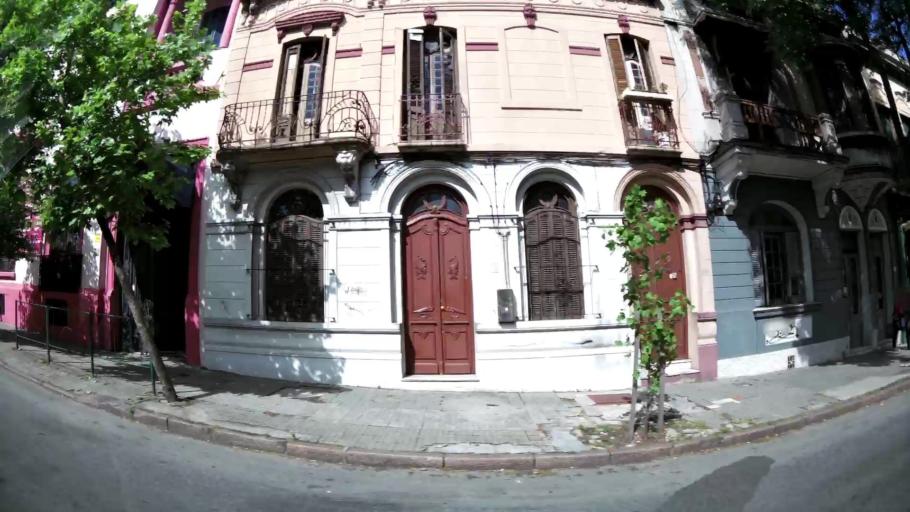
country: UY
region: Montevideo
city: Montevideo
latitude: -34.8789
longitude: -56.1961
